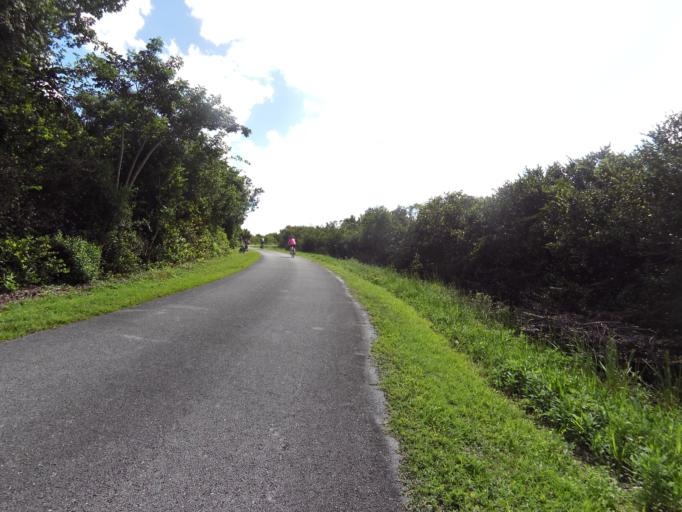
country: US
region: Florida
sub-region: Miami-Dade County
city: The Hammocks
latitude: 25.7246
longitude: -80.7670
